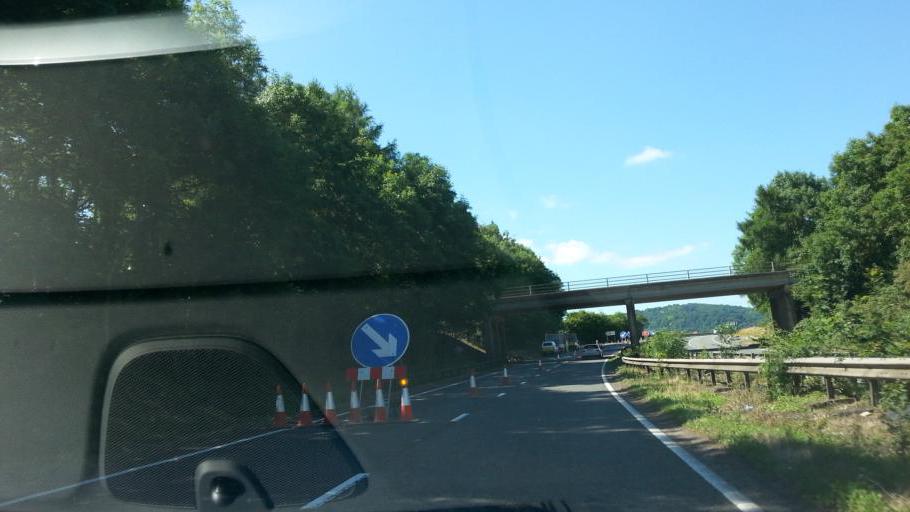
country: GB
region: England
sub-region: Herefordshire
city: Marstow
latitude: 51.8688
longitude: -2.6307
